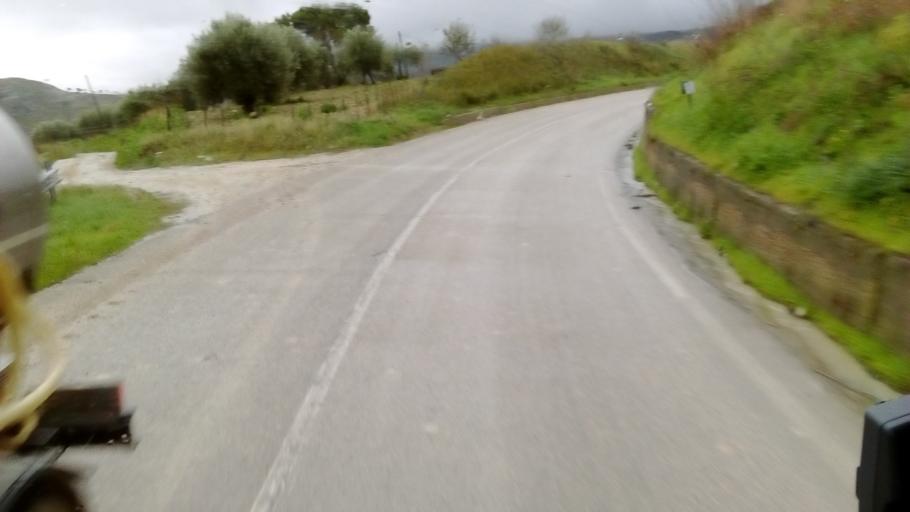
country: IT
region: Sicily
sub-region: Enna
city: Pietraperzia
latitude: 37.4509
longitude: 14.1767
